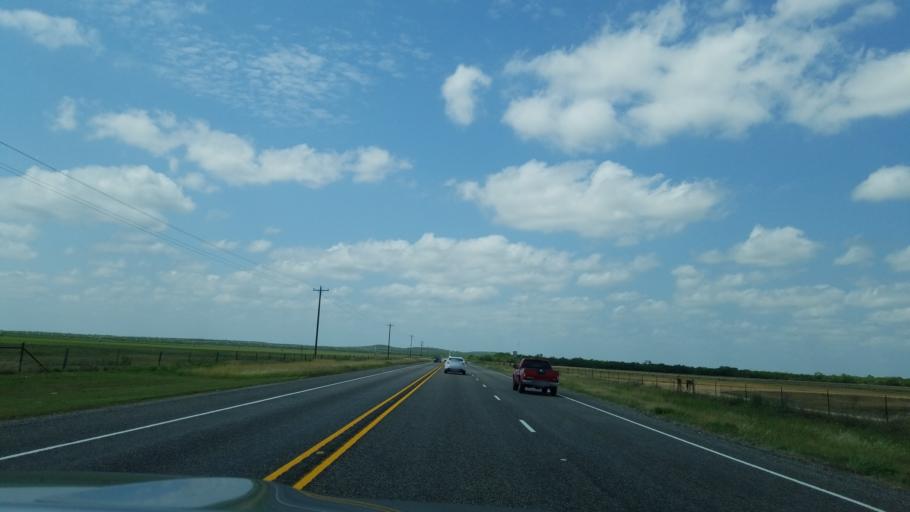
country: US
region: Texas
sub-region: Frio County
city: Pearsall
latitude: 28.9624
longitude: -99.2540
